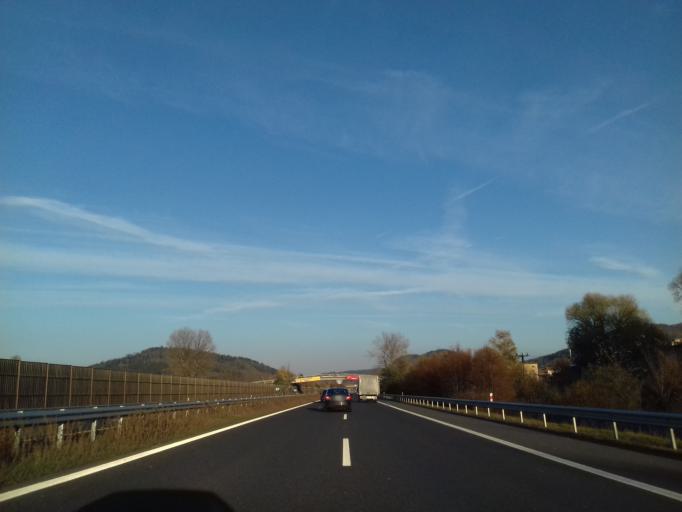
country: CZ
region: Central Bohemia
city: Zdice
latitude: 49.9062
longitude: 13.9711
